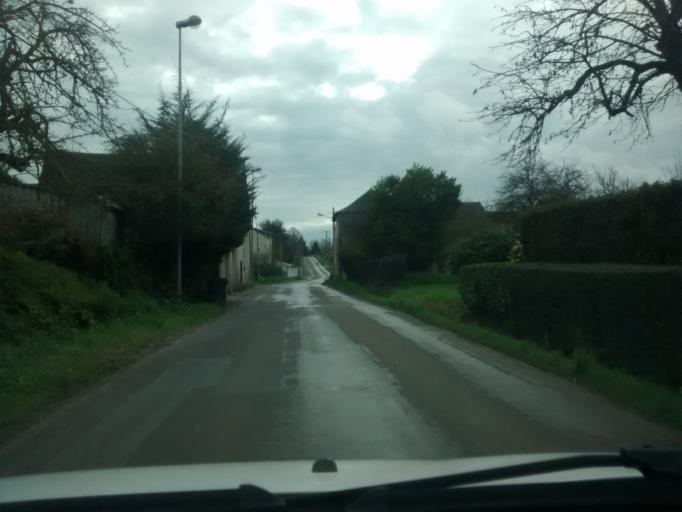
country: FR
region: Brittany
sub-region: Departement d'Ille-et-Vilaine
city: Cesson-Sevigne
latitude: 48.1354
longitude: -1.5993
